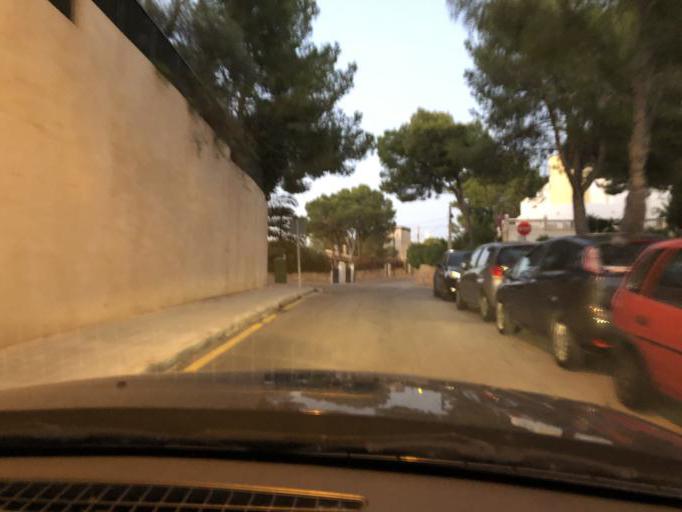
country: ES
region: Balearic Islands
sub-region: Illes Balears
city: Santa Ponsa
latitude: 39.5207
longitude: 2.4758
